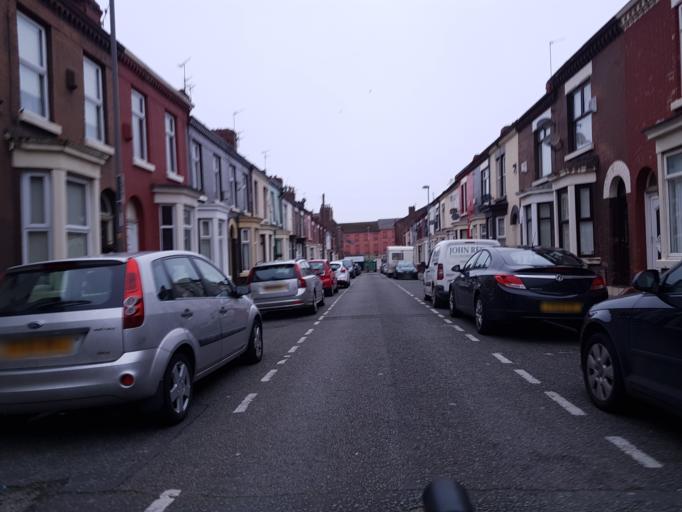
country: GB
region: England
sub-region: Liverpool
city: Liverpool
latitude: 53.4389
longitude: -2.9694
